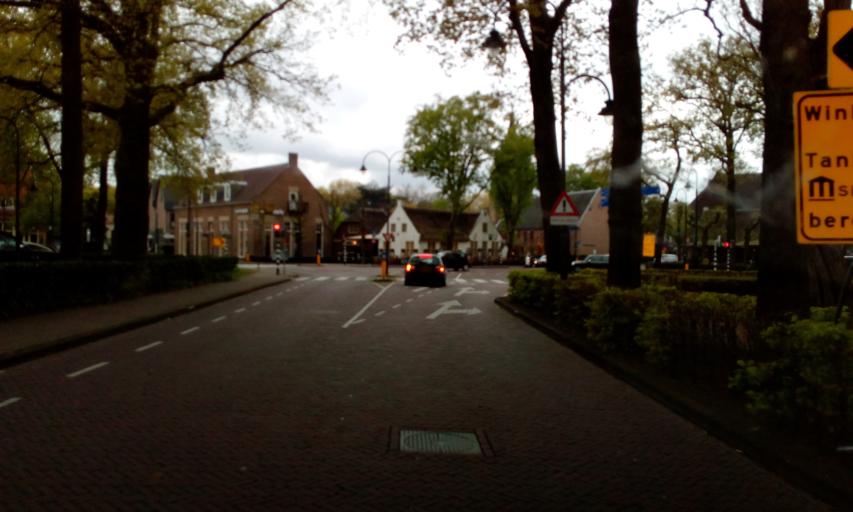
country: NL
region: North Holland
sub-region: Gemeente Laren
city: Laren
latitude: 52.2565
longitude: 5.2250
